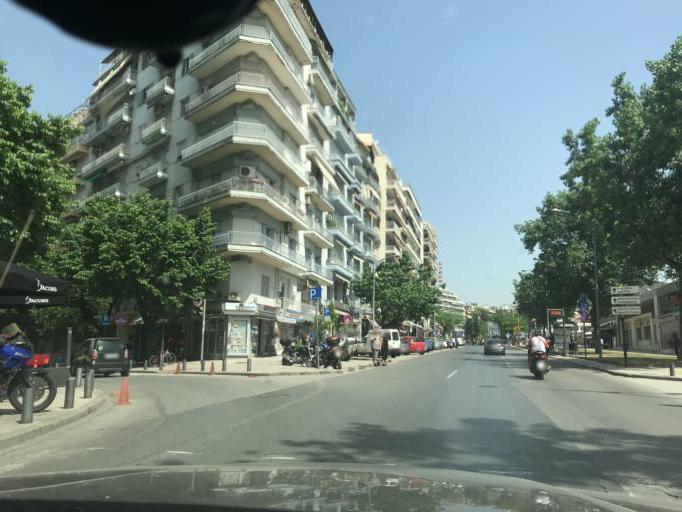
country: GR
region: Central Macedonia
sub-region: Nomos Thessalonikis
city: Agios Pavlos
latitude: 40.6293
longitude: 22.9533
